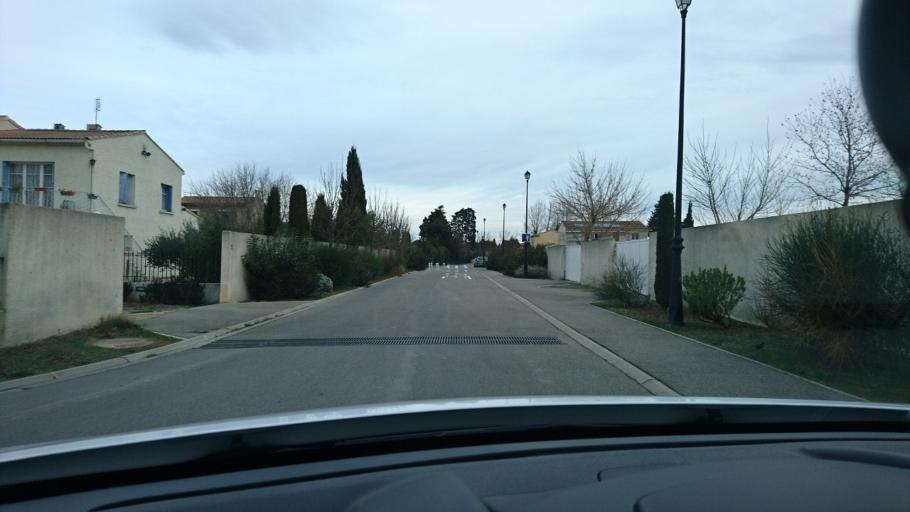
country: FR
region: Provence-Alpes-Cote d'Azur
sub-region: Departement des Bouches-du-Rhone
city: Rognonas
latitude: 43.9021
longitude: 4.7994
